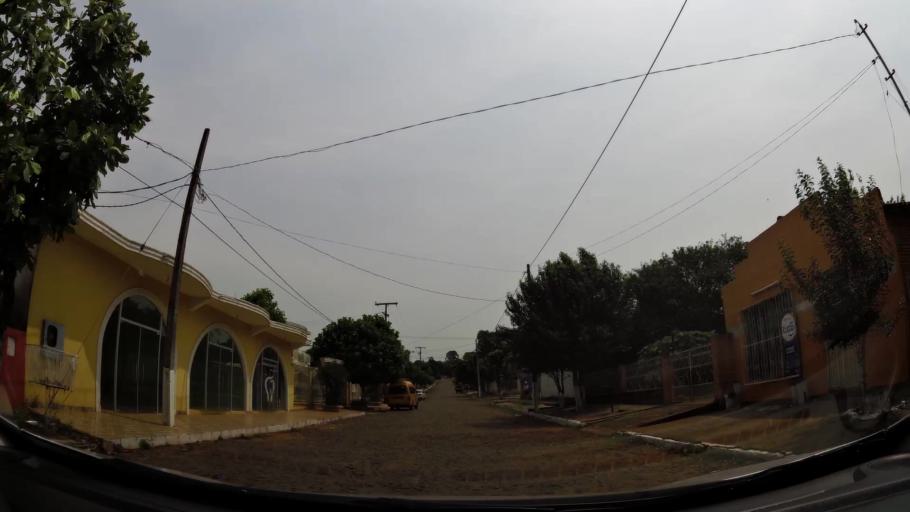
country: BR
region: Parana
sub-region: Foz Do Iguacu
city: Foz do Iguacu
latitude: -25.5654
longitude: -54.6039
